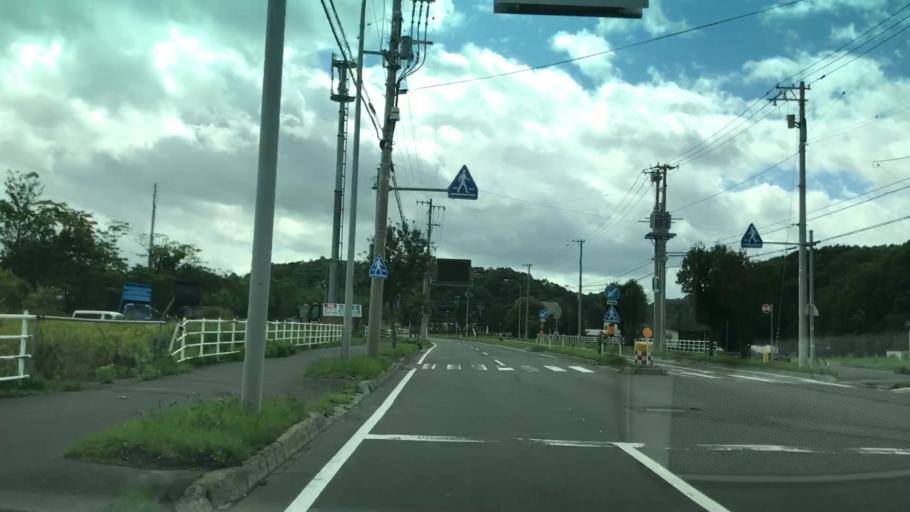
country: JP
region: Hokkaido
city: Sapporo
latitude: 42.9811
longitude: 141.4384
